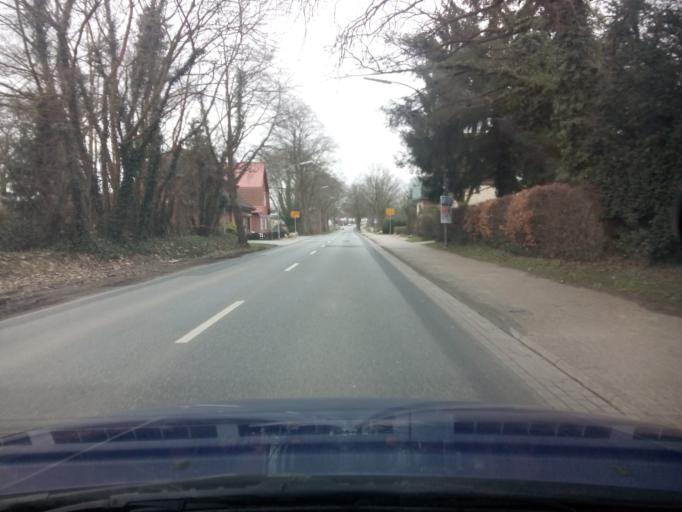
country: DE
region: Lower Saxony
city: Osterholz-Scharmbeck
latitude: 53.2397
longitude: 8.8132
